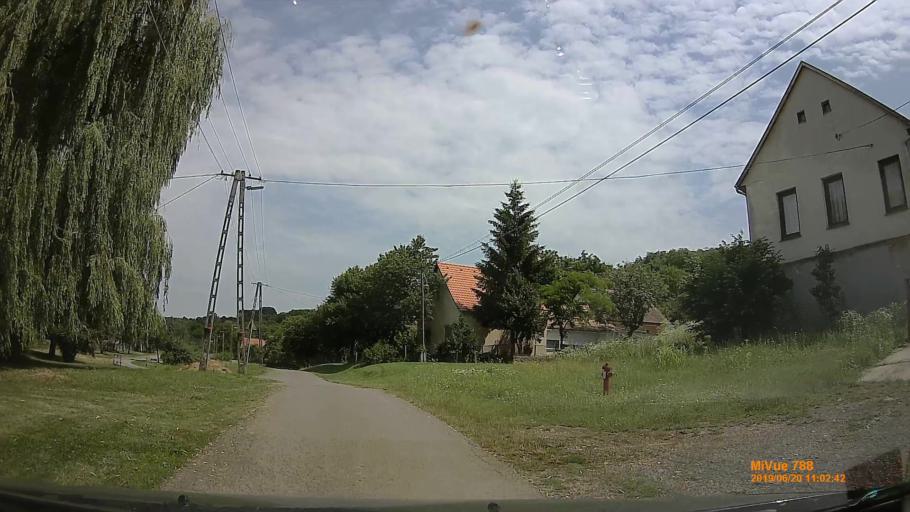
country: HU
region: Baranya
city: Mecseknadasd
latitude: 46.1794
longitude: 18.5118
